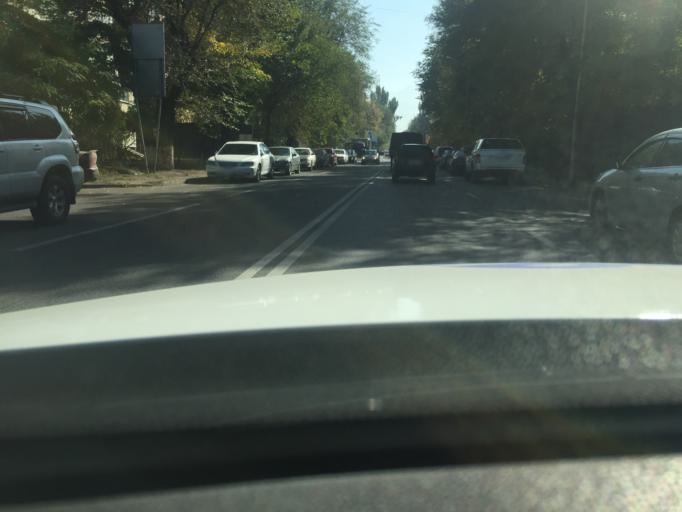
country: KZ
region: Almaty Qalasy
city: Almaty
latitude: 43.2541
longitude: 76.9113
